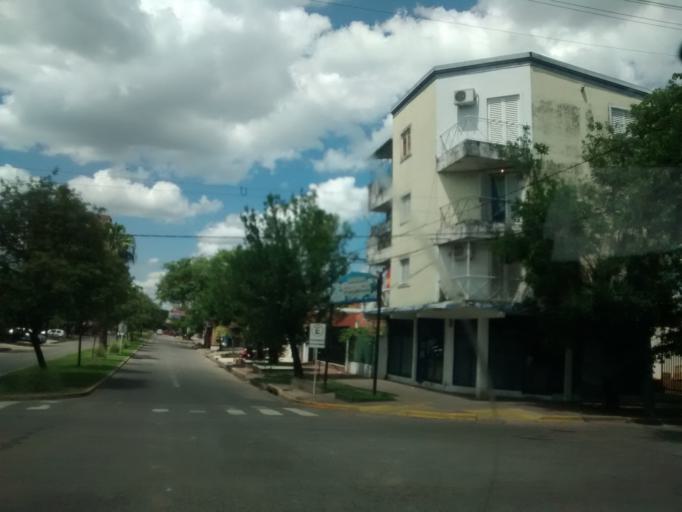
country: AR
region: Chaco
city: Resistencia
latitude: -27.4551
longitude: -58.9909
